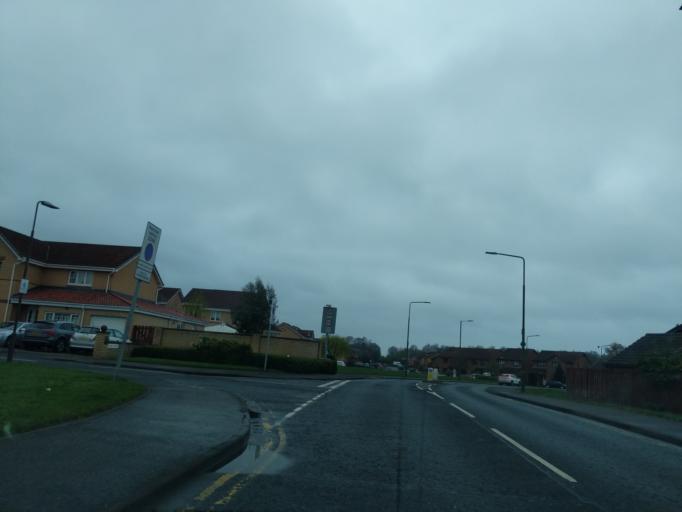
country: GB
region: Scotland
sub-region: East Lothian
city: Musselburgh
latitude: 55.9356
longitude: -3.0732
